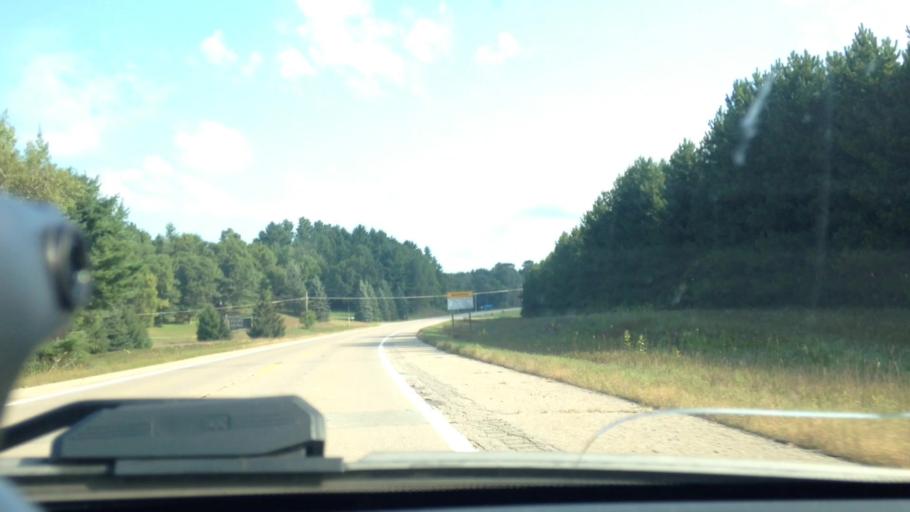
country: US
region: Michigan
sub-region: Dickinson County
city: Norway
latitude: 45.7599
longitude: -87.9214
